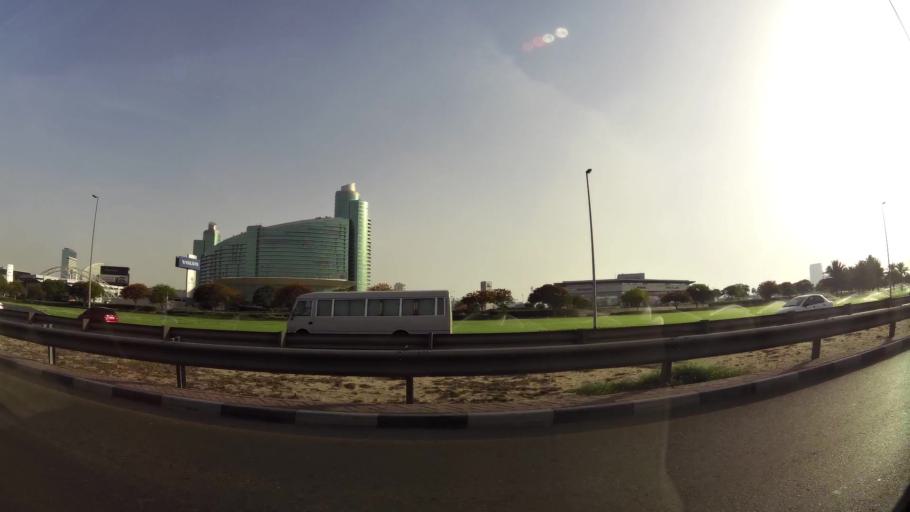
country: AE
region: Ash Shariqah
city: Sharjah
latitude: 25.2355
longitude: 55.3482
